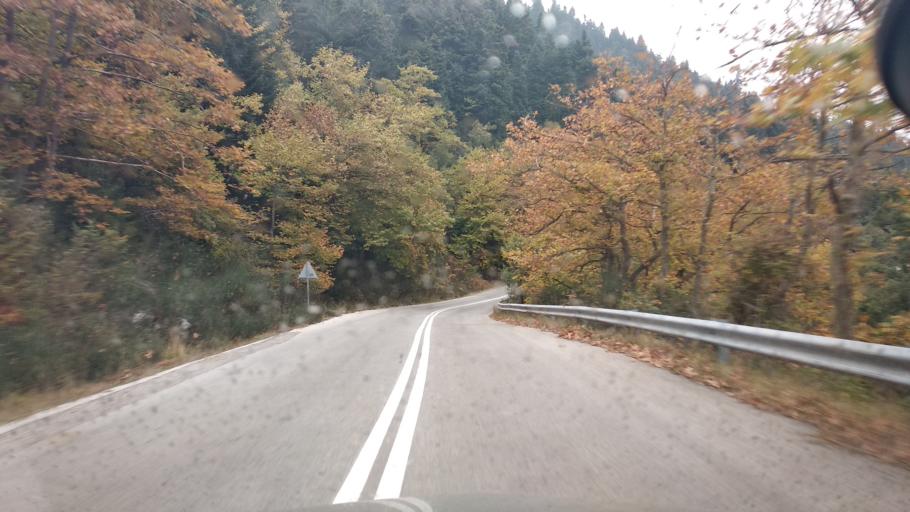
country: GR
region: Thessaly
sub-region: Trikala
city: Pyli
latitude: 39.5101
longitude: 21.5327
